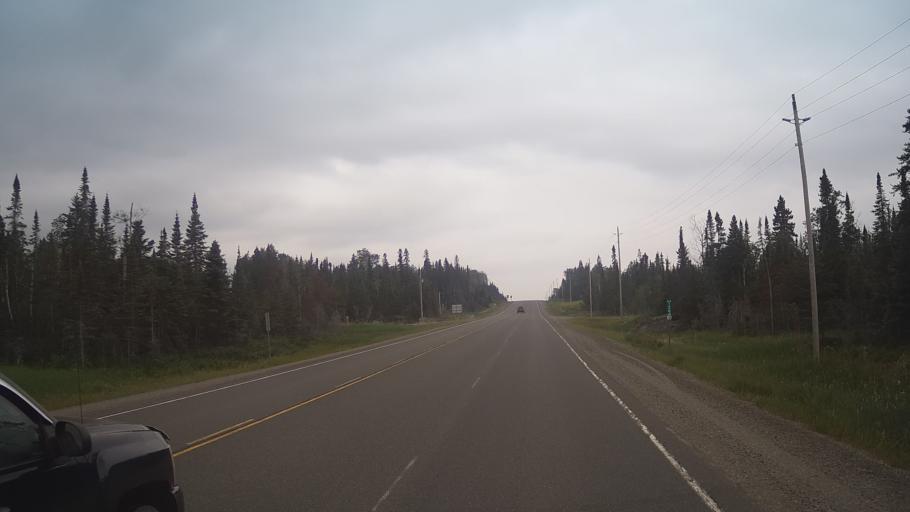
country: CA
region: Ontario
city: Greenstone
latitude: 49.5620
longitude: -87.9792
